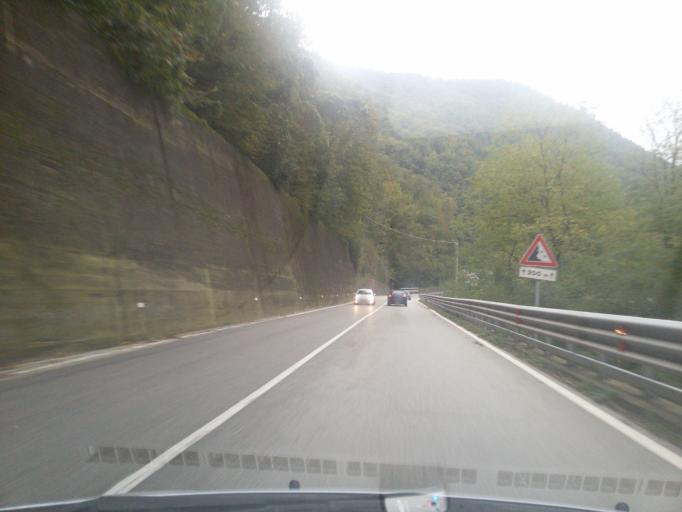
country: IT
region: Liguria
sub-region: Provincia di Genova
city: Davagna
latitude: 44.4409
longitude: 9.0460
